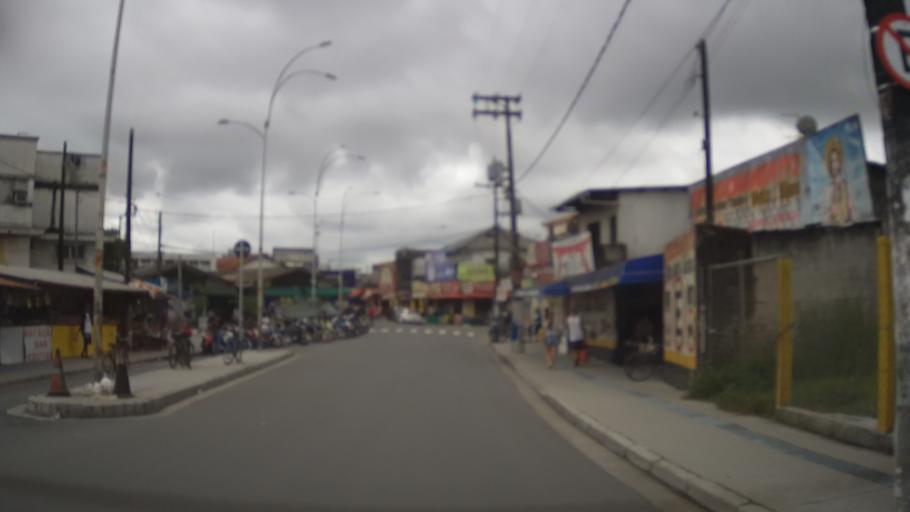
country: BR
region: Sao Paulo
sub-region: Santos
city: Santos
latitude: -23.9402
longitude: -46.3072
